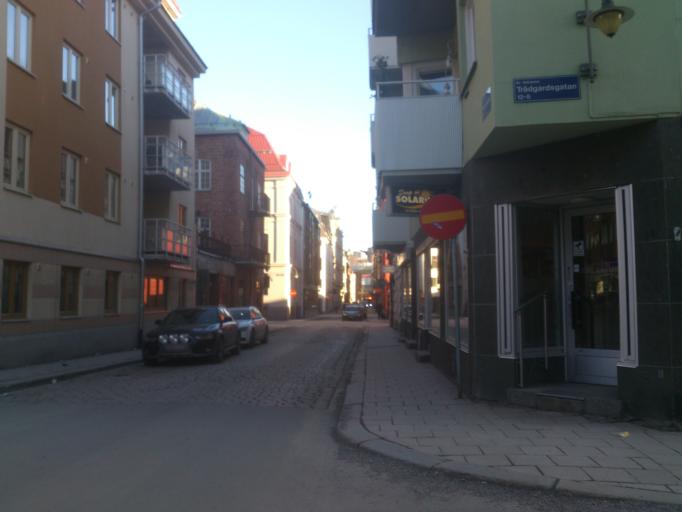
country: SE
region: Vaesternorrland
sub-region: Sundsvalls Kommun
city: Sundsvall
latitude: 62.3889
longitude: 17.3108
